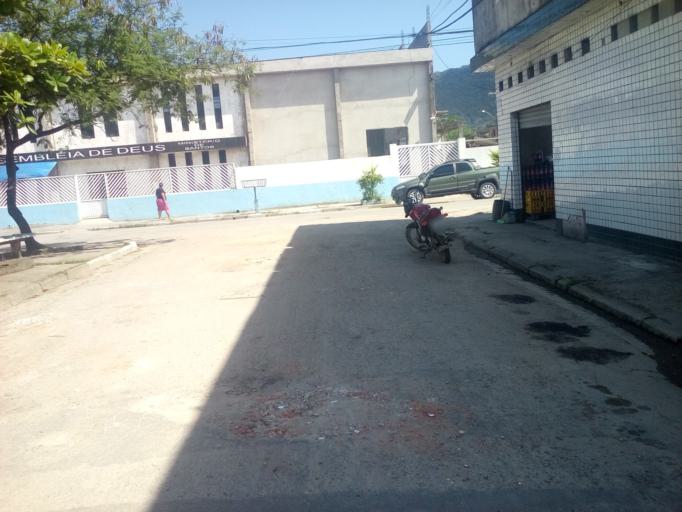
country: BR
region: Sao Paulo
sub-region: Guaruja
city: Guaruja
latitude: -23.9641
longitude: -46.2578
